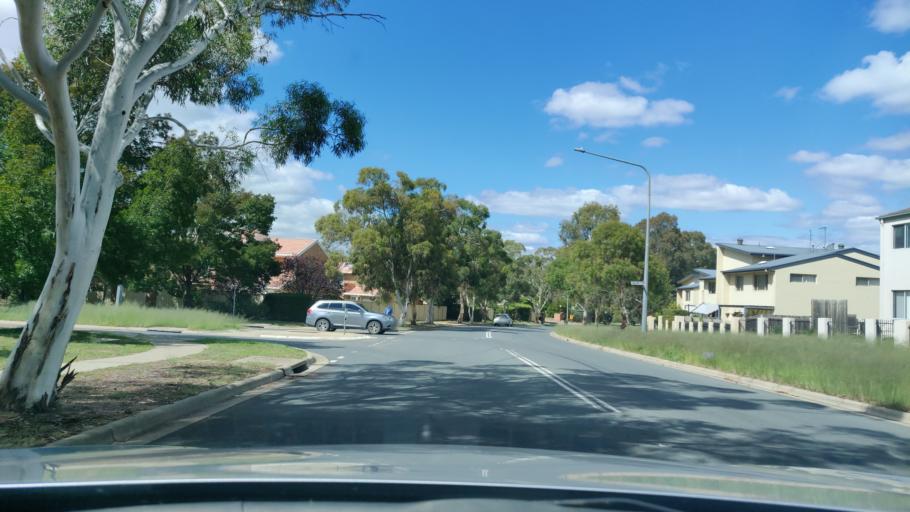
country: AU
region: Australian Capital Territory
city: Macarthur
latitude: -35.4264
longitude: 149.0735
